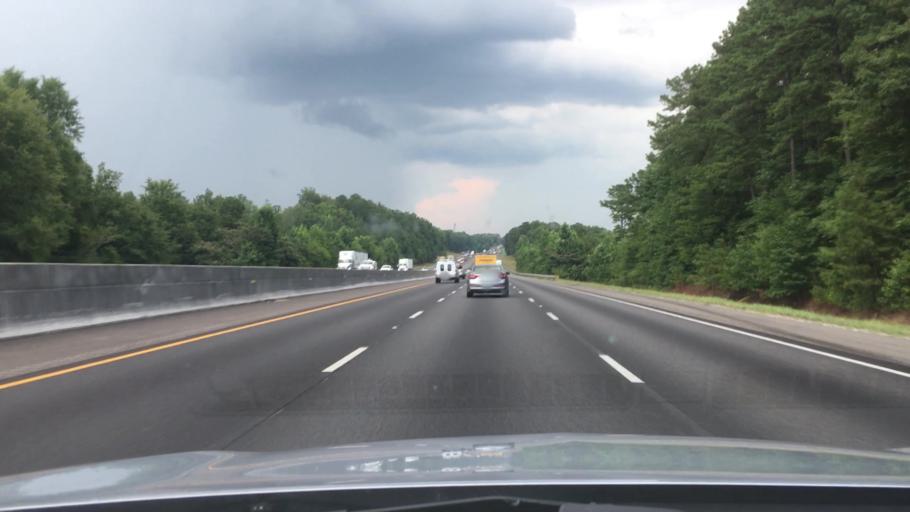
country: US
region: Alabama
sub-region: Bibb County
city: North Bibb
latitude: 33.2244
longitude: -87.1770
